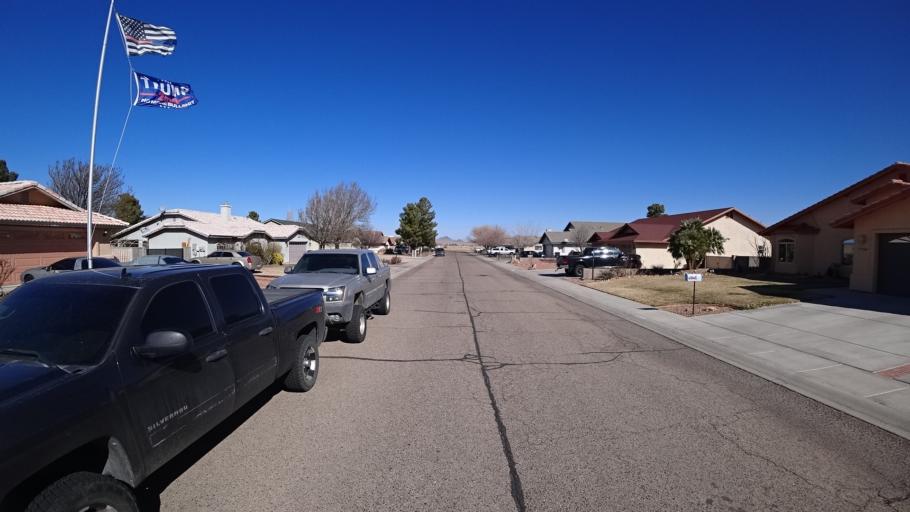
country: US
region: Arizona
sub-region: Mohave County
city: New Kingman-Butler
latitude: 35.2378
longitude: -114.0017
